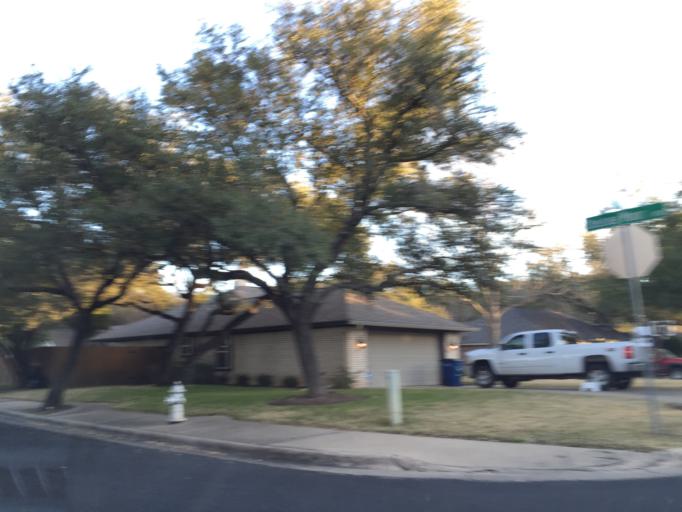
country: US
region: Texas
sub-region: Williamson County
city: Jollyville
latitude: 30.4263
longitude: -97.7653
